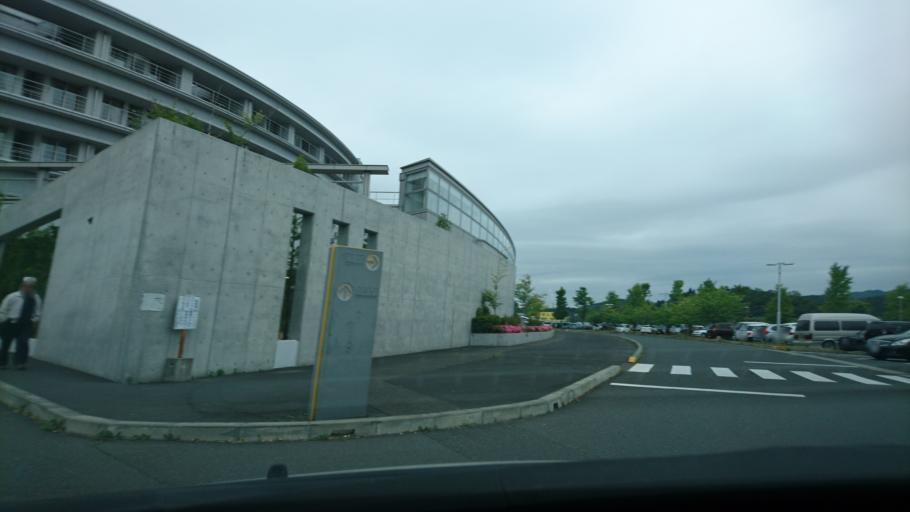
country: JP
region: Iwate
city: Ichinoseki
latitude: 38.9348
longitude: 141.1694
